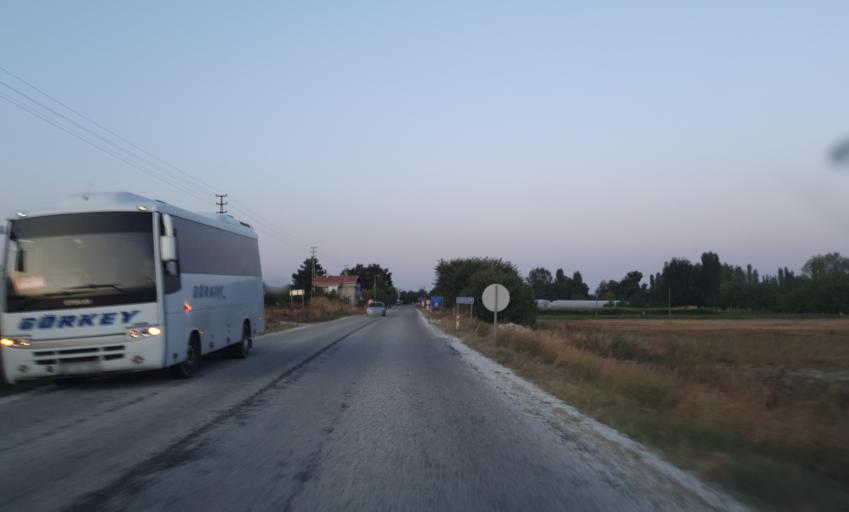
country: TR
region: Kirklareli
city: Pinarhisar
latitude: 41.6262
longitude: 27.5655
